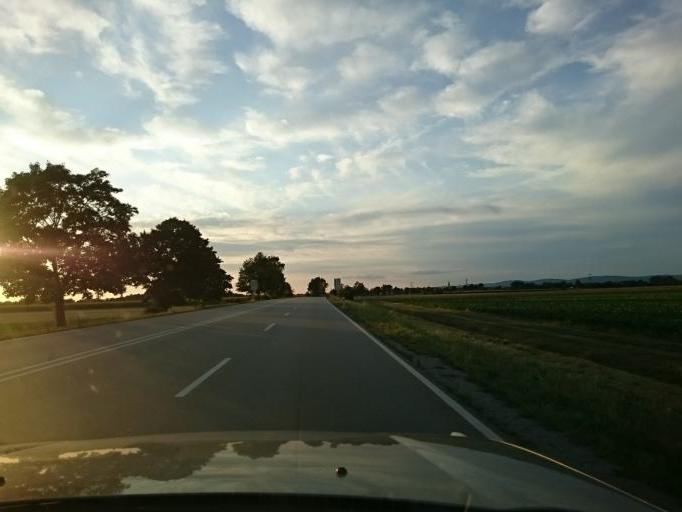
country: DE
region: Bavaria
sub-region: Lower Bavaria
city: Alterhofen
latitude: 48.8309
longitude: 12.6301
